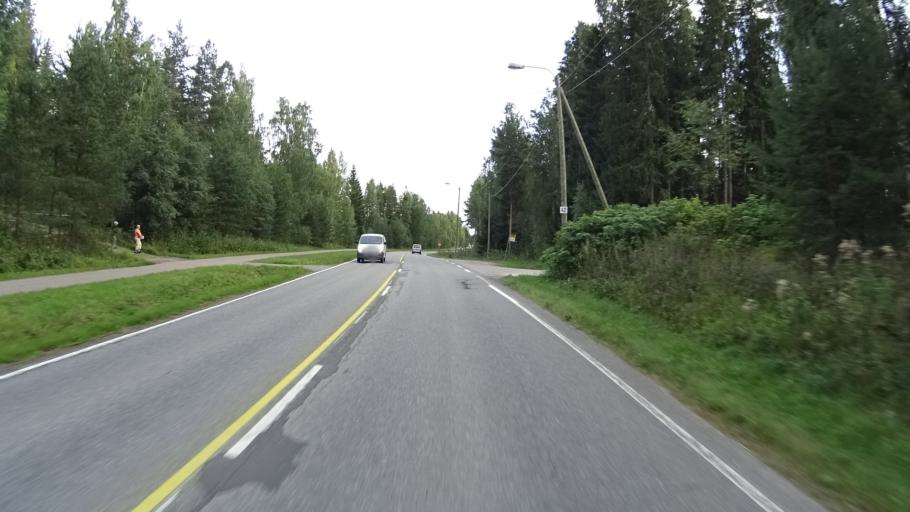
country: FI
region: Uusimaa
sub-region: Helsinki
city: Nurmijaervi
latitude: 60.3399
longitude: 24.8647
